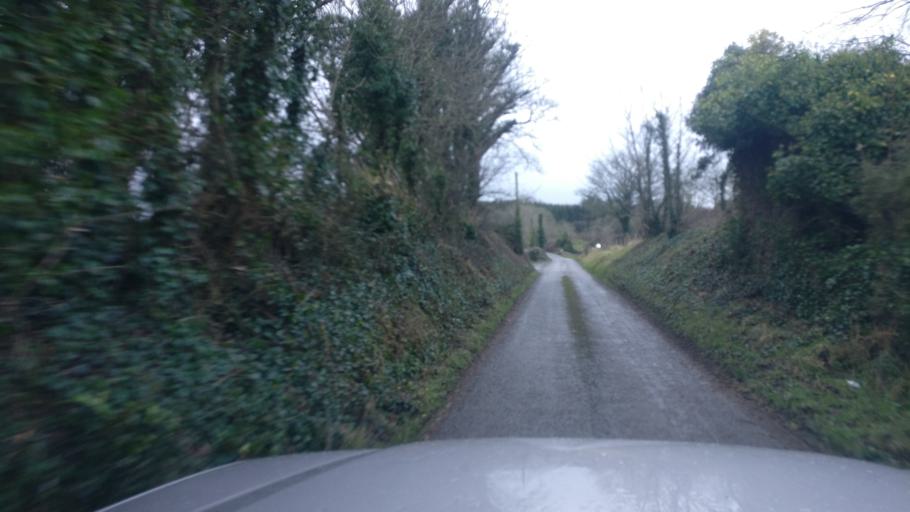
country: IE
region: Connaught
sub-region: County Galway
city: Athenry
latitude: 53.1884
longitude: -8.6933
